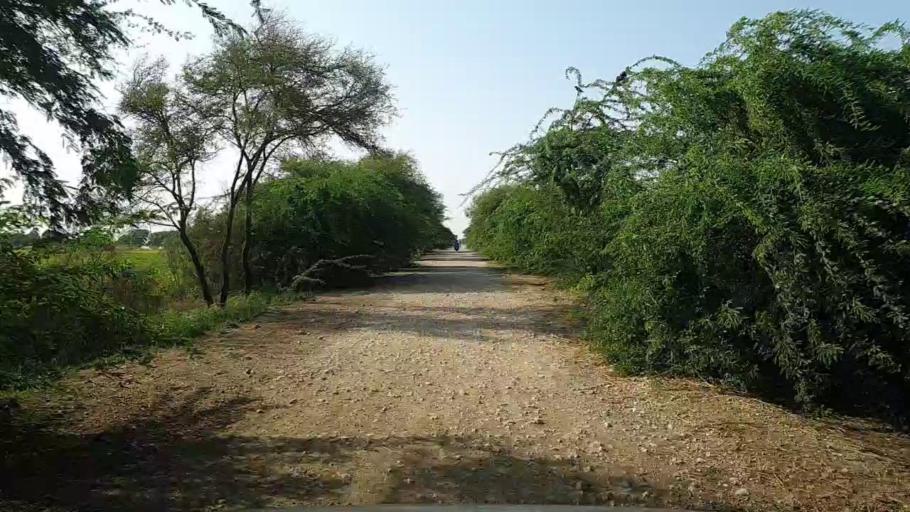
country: PK
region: Sindh
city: Kario
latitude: 24.8130
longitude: 68.5032
